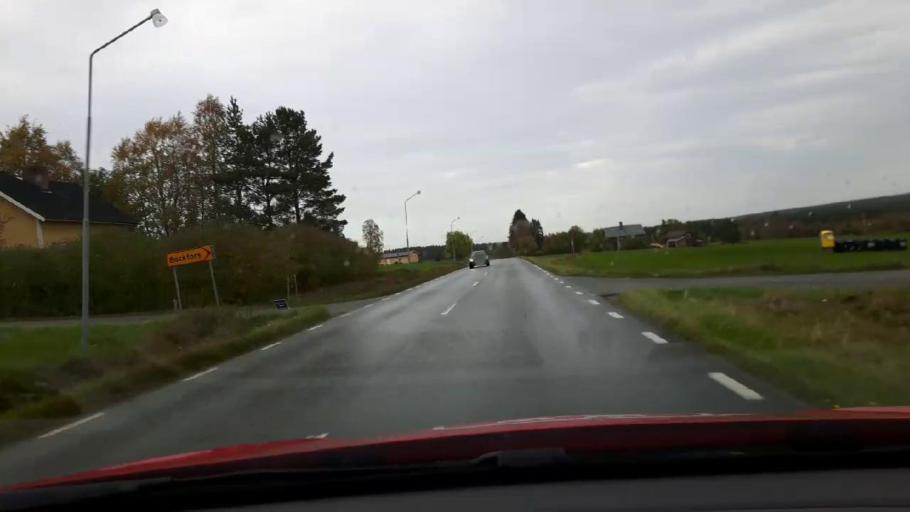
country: SE
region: Jaemtland
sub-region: Bergs Kommun
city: Hoverberg
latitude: 63.0173
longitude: 14.3438
